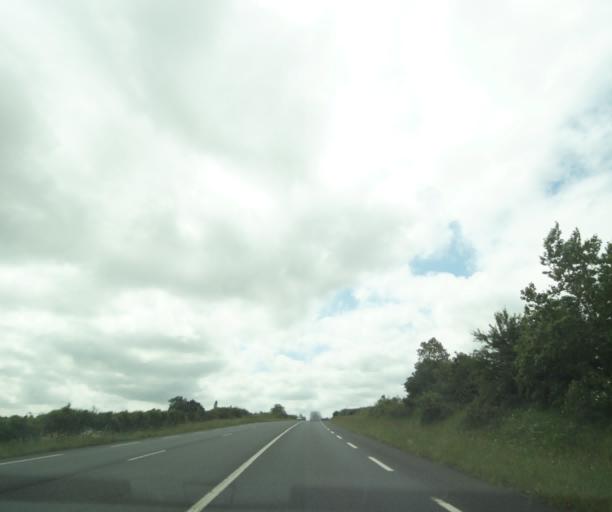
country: FR
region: Poitou-Charentes
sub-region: Departement des Deux-Sevres
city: Viennay
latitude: 46.7535
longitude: -0.2243
